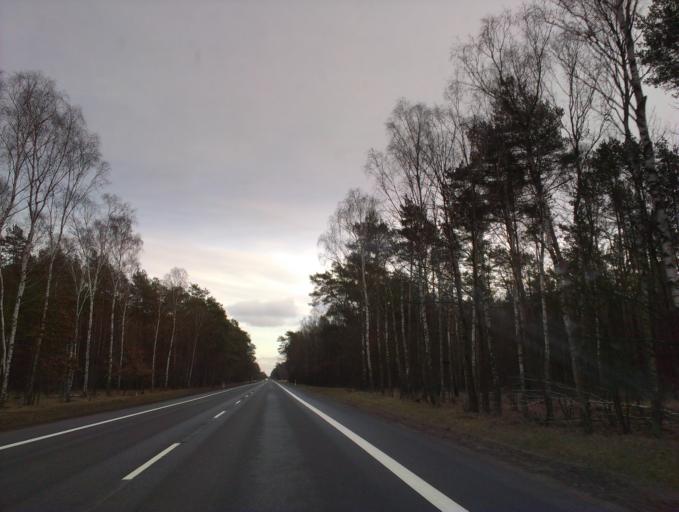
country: PL
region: Masovian Voivodeship
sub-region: Powiat sierpecki
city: Szczutowo
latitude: 52.8797
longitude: 19.5978
